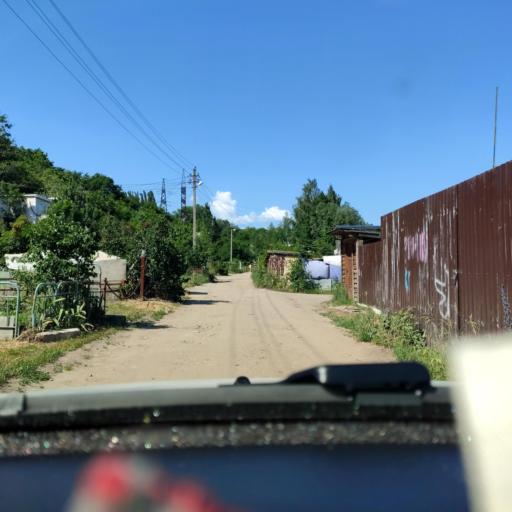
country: RU
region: Voronezj
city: Voronezh
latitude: 51.6209
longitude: 39.1926
